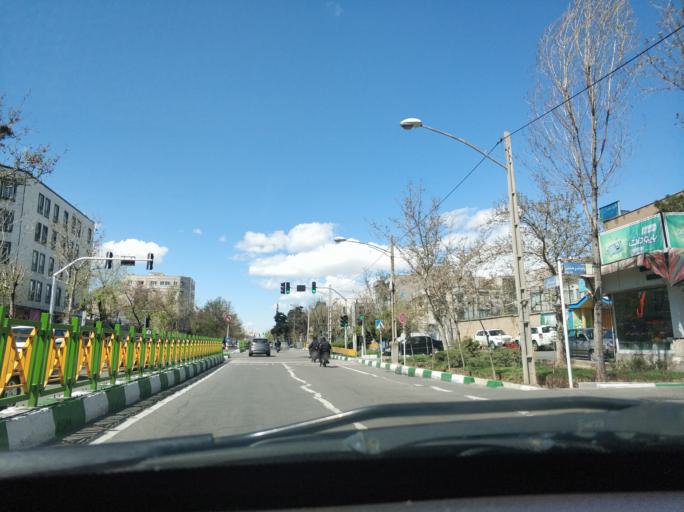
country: IR
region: Tehran
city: Tehran
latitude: 35.7206
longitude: 51.4882
